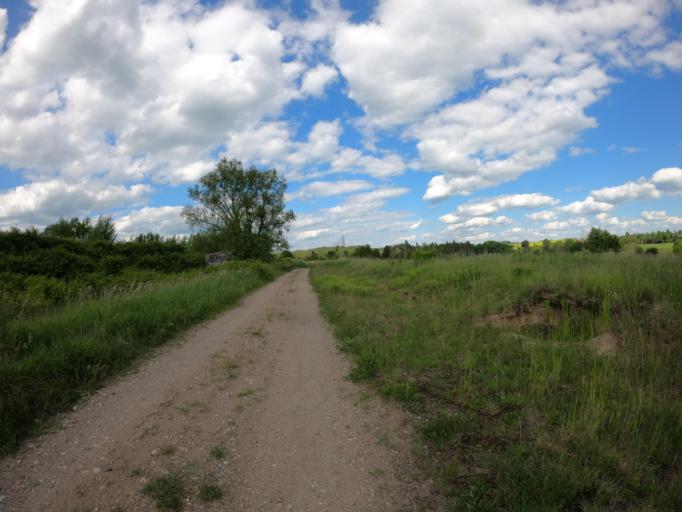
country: PL
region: Warmian-Masurian Voivodeship
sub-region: Powiat lidzbarski
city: Lidzbark Warminski
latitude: 54.1411
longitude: 20.6030
